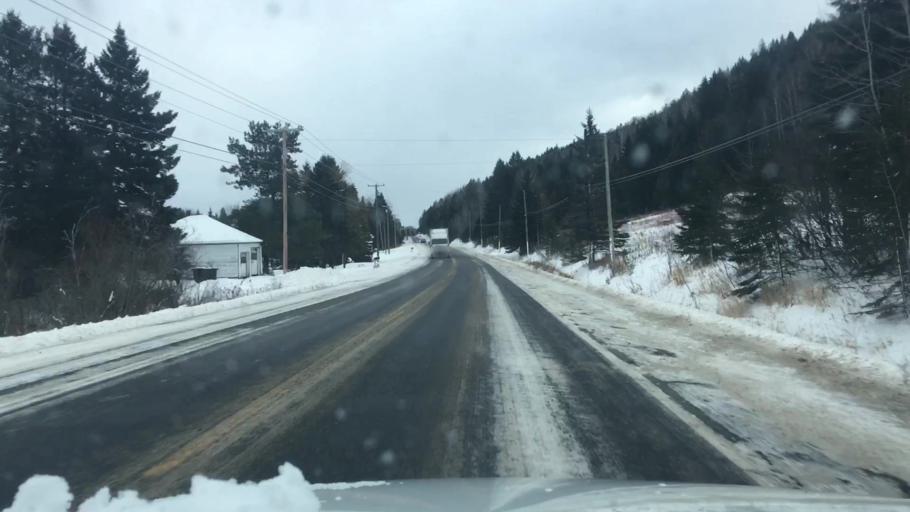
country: US
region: Maine
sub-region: Aroostook County
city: Madawaska
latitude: 47.3311
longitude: -68.2007
